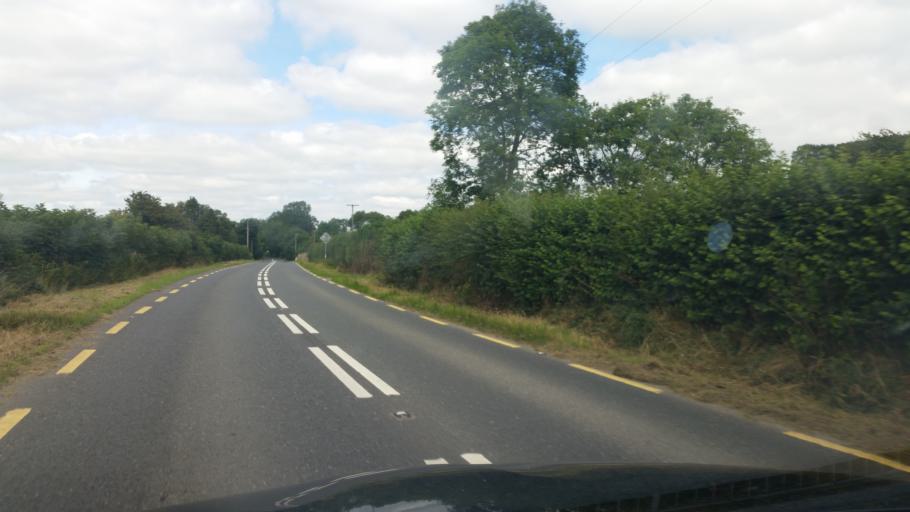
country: IE
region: Leinster
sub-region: Wicklow
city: Baltinglass
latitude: 52.9607
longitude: -6.6985
